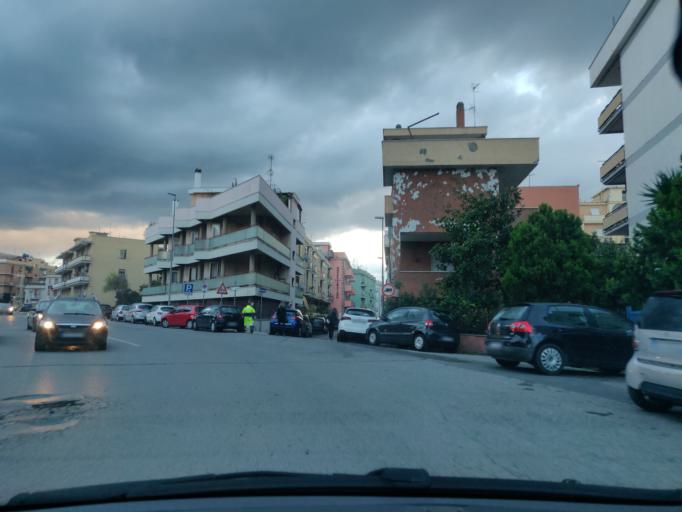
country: IT
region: Latium
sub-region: Citta metropolitana di Roma Capitale
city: Civitavecchia
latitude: 42.0948
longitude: 11.8039
